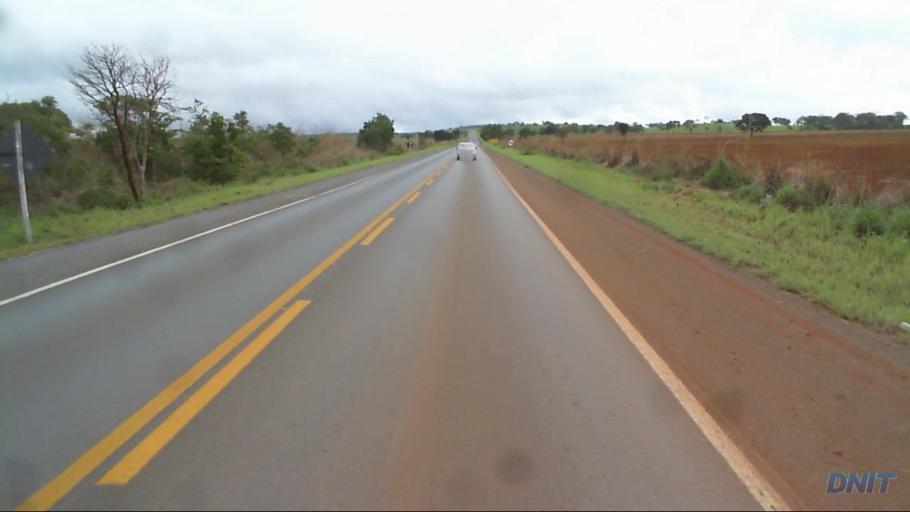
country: BR
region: Goias
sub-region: Padre Bernardo
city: Padre Bernardo
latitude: -15.2208
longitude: -48.5452
